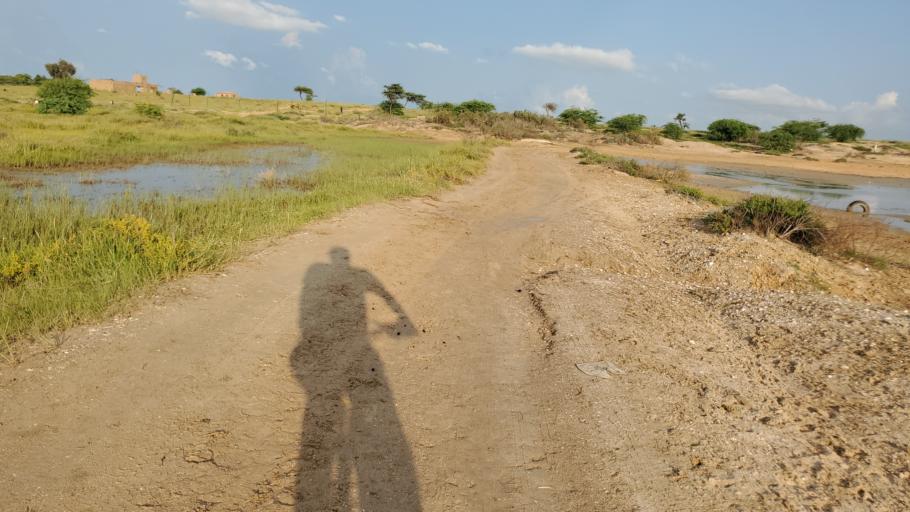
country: SN
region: Saint-Louis
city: Saint-Louis
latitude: 16.0488
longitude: -16.4170
